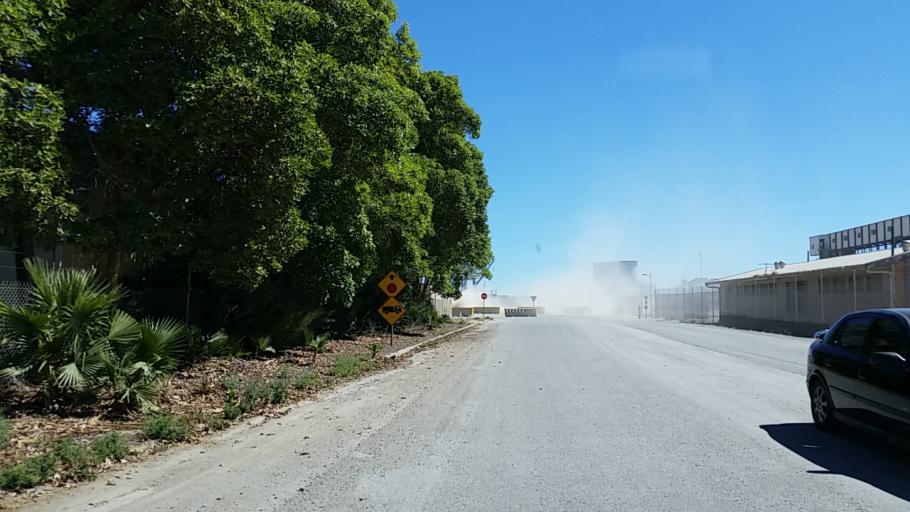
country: AU
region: South Australia
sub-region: Port Adelaide Enfield
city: Birkenhead
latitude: -34.8271
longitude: 138.5108
